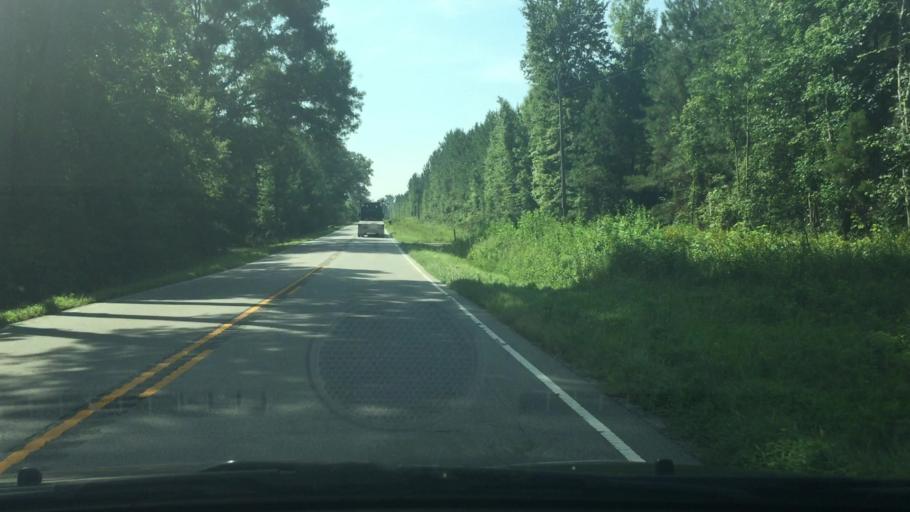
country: US
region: Virginia
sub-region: Sussex County
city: Sussex
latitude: 36.8649
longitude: -77.1400
